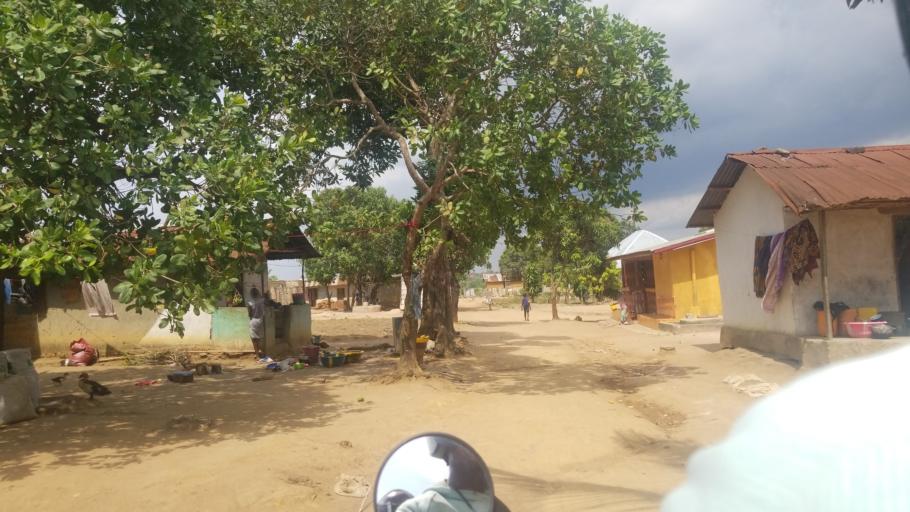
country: SL
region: Western Area
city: Waterloo
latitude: 8.3168
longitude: -13.0458
